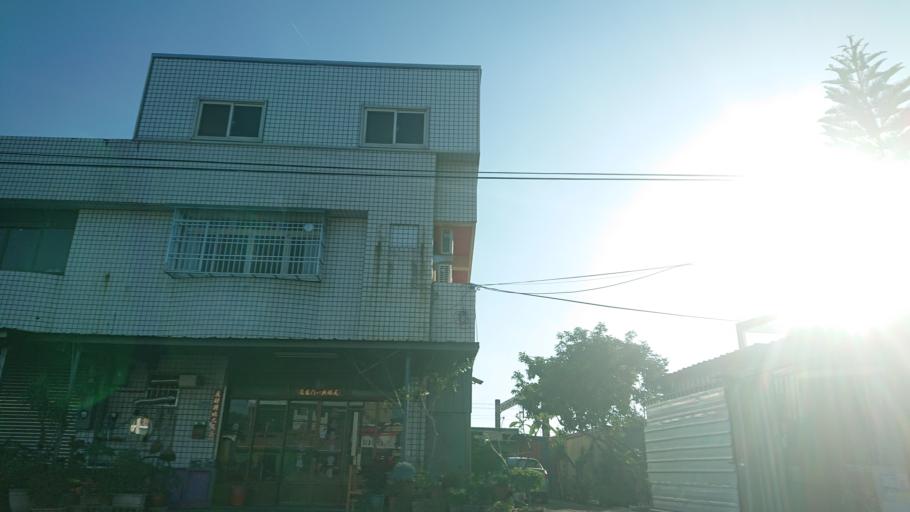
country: TW
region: Taiwan
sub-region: Changhua
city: Chang-hua
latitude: 24.1203
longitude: 120.5723
